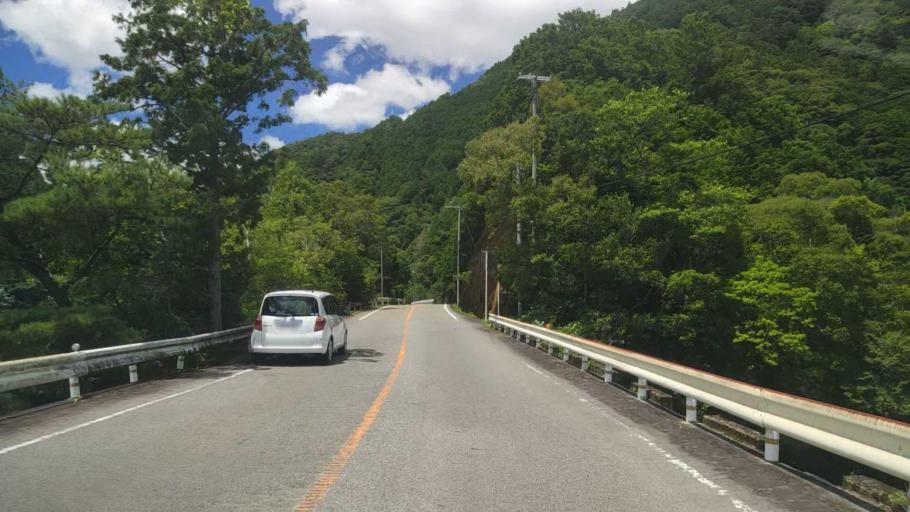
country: JP
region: Mie
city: Owase
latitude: 33.9965
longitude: 136.0242
